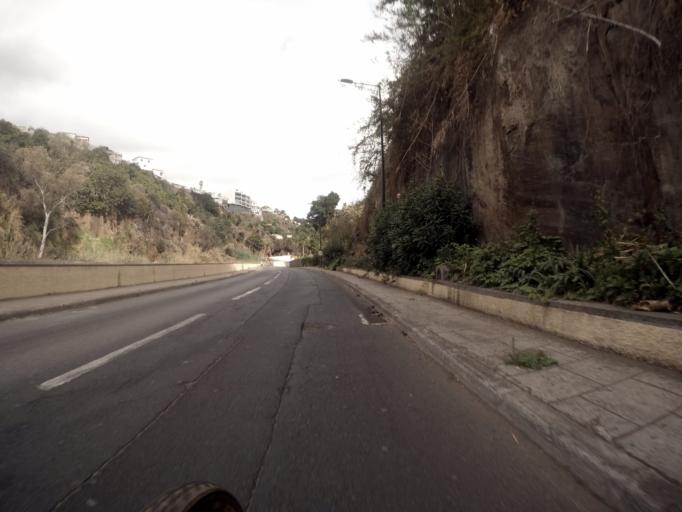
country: PT
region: Madeira
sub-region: Funchal
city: Nossa Senhora do Monte
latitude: 32.6573
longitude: -16.9242
